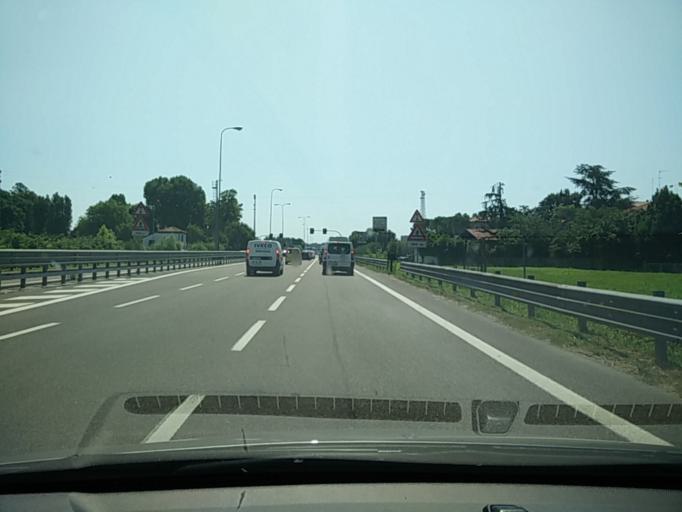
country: IT
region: Veneto
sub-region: Provincia di Venezia
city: Campalto
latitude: 45.5109
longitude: 12.2614
